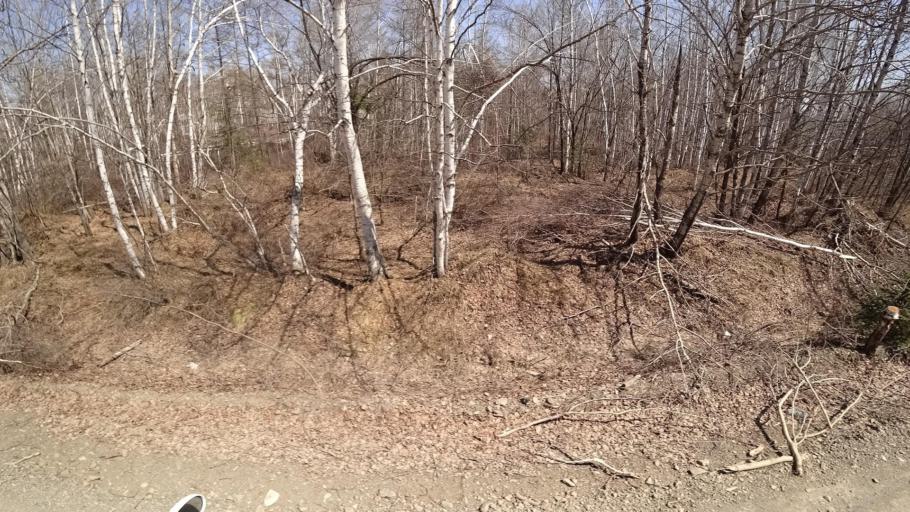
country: RU
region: Khabarovsk Krai
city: Khurba
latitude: 50.4132
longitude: 136.8419
